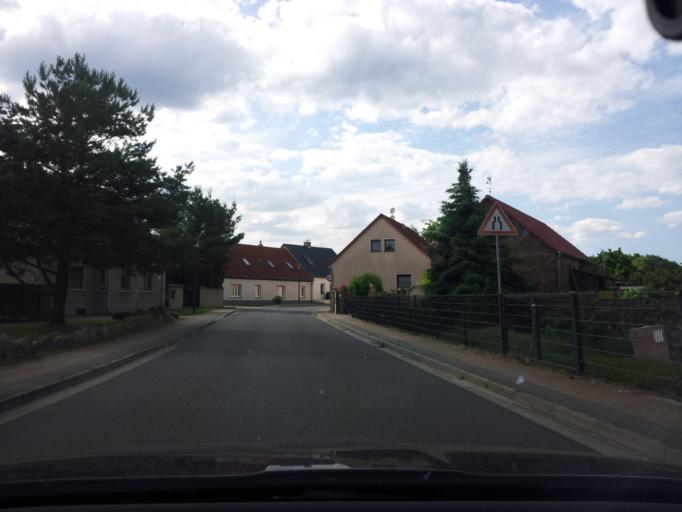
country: DE
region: Brandenburg
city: Juterbog
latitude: 52.0180
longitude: 13.0585
